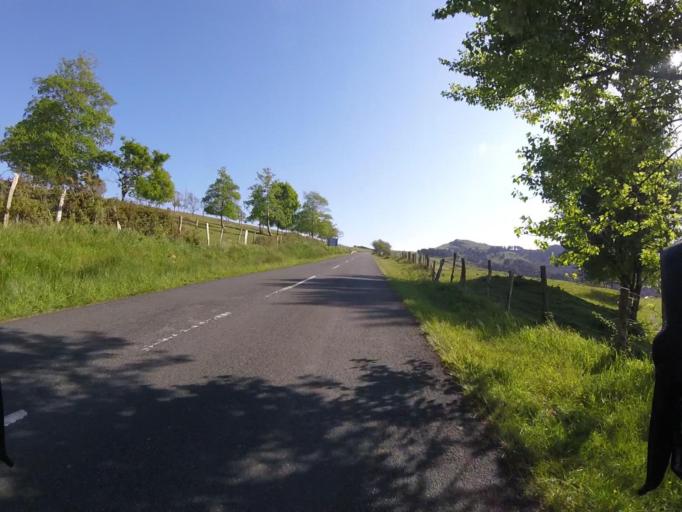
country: ES
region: Basque Country
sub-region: Provincia de Guipuzcoa
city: Fuenterrabia
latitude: 43.3588
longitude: -1.8398
